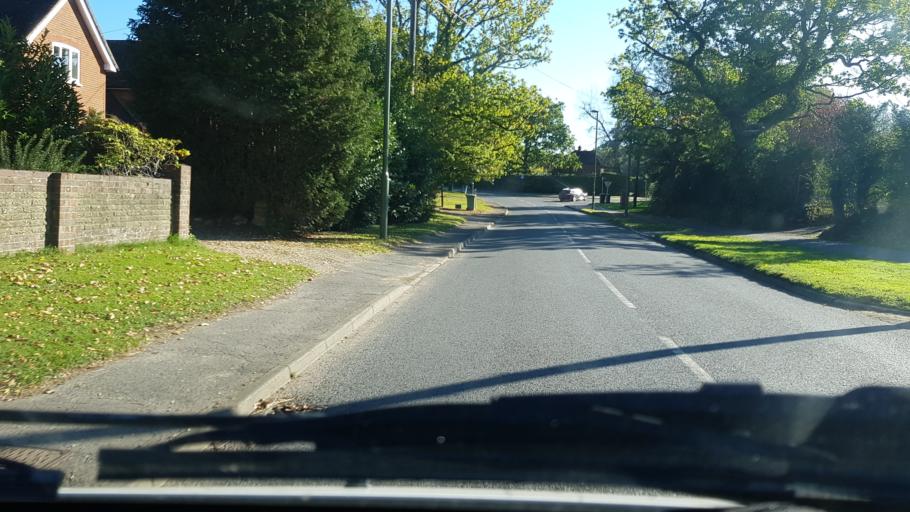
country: GB
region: England
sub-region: Surrey
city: Cranleigh
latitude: 51.1461
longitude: -0.4713
